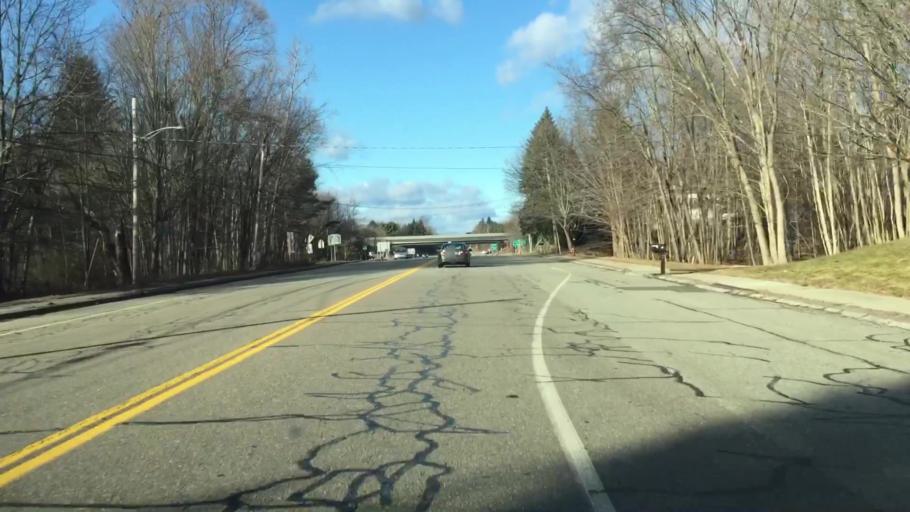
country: US
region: Massachusetts
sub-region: Worcester County
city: West Boylston
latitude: 42.3998
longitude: -71.7959
